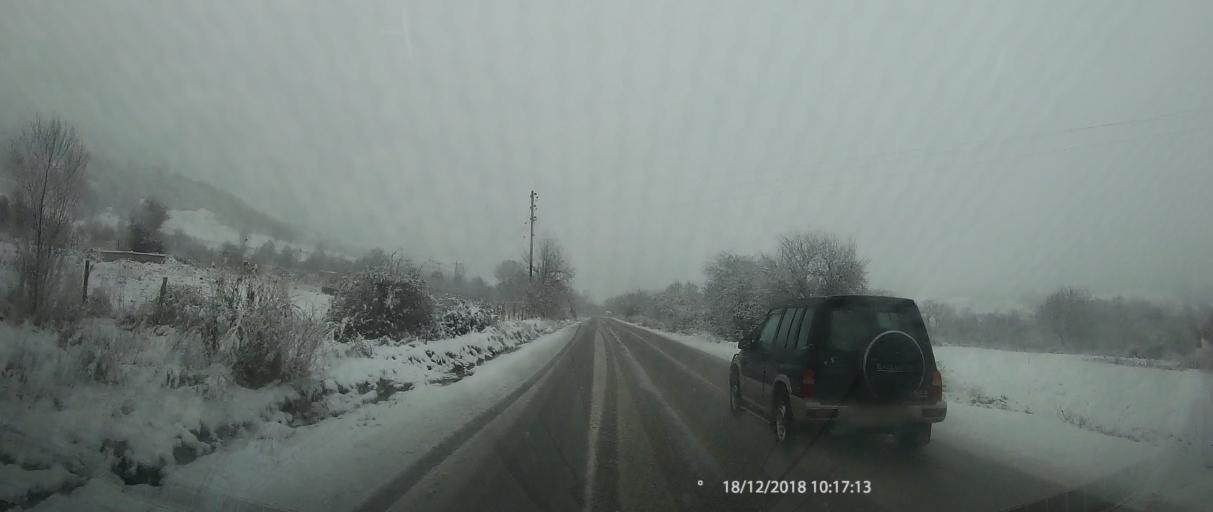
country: GR
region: Thessaly
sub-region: Nomos Larisis
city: Livadi
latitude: 40.1221
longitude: 22.2118
